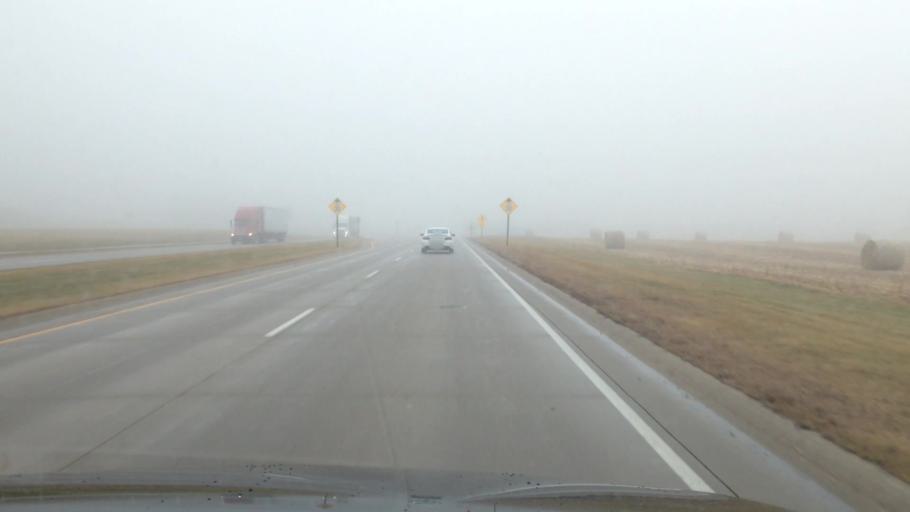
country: US
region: Wisconsin
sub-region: Walworth County
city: Lake Geneva
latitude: 42.5790
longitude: -88.4115
